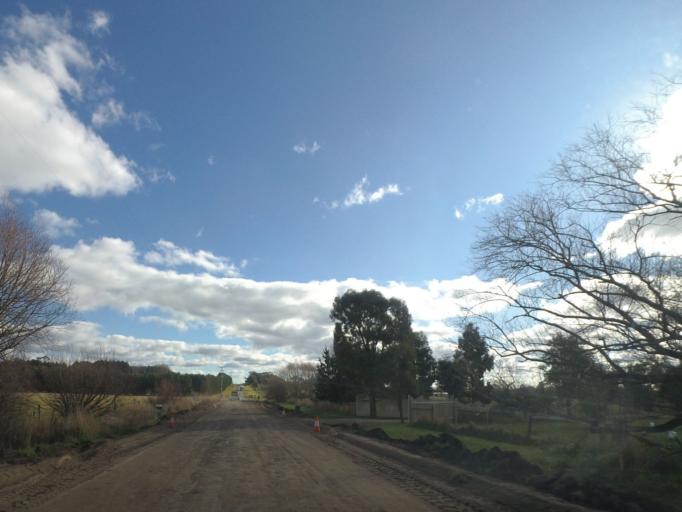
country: AU
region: Victoria
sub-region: Mount Alexander
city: Castlemaine
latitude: -37.2546
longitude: 144.4291
